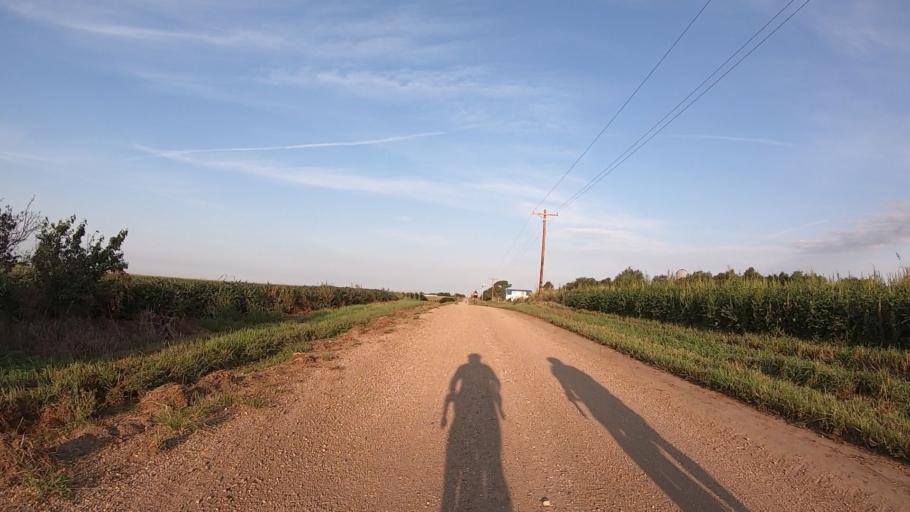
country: US
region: Kansas
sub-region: Marshall County
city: Marysville
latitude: 39.7694
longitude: -96.7360
